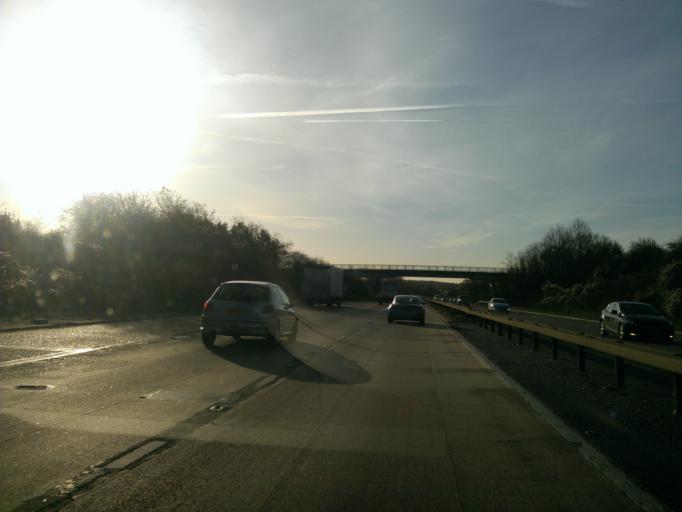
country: GB
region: England
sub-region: Essex
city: Kelvedon
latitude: 51.8448
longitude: 0.7241
